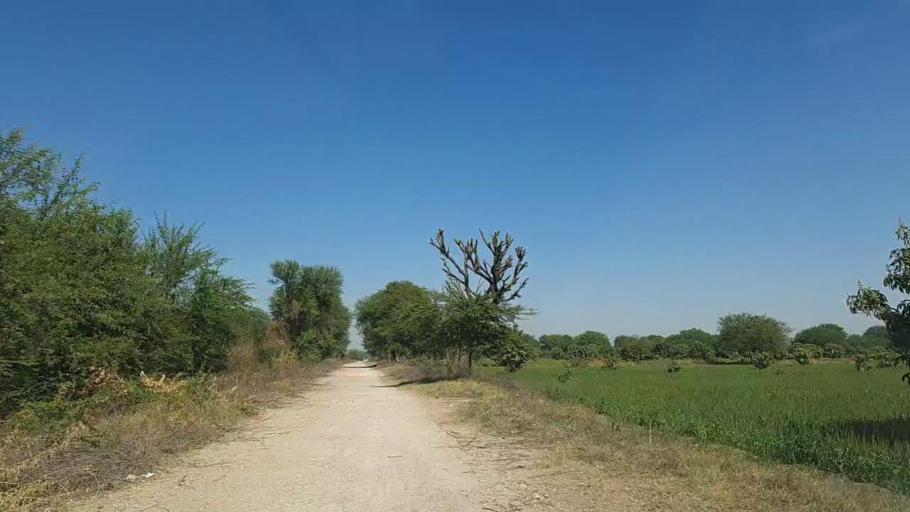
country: PK
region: Sindh
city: Samaro
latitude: 25.3580
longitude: 69.5230
